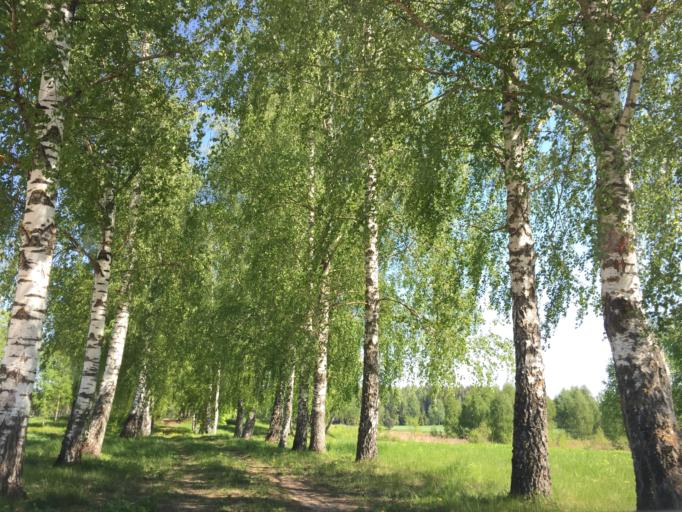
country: LV
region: Ikskile
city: Ikskile
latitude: 56.8579
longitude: 24.5034
